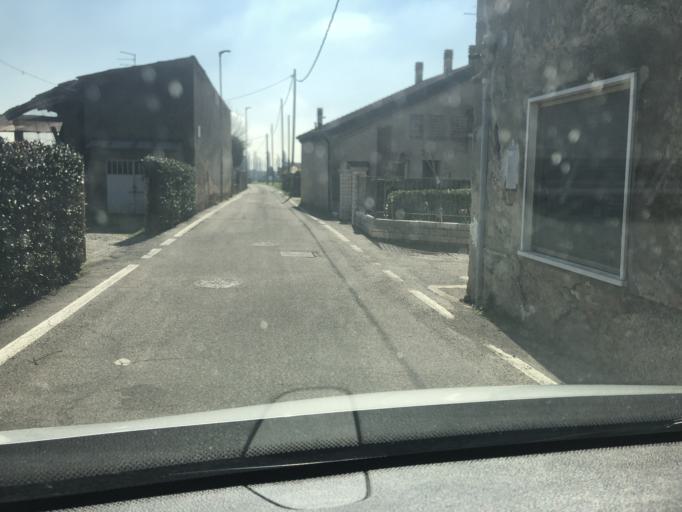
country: IT
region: Veneto
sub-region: Provincia di Verona
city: Villafranca di Verona
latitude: 45.3744
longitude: 10.8241
